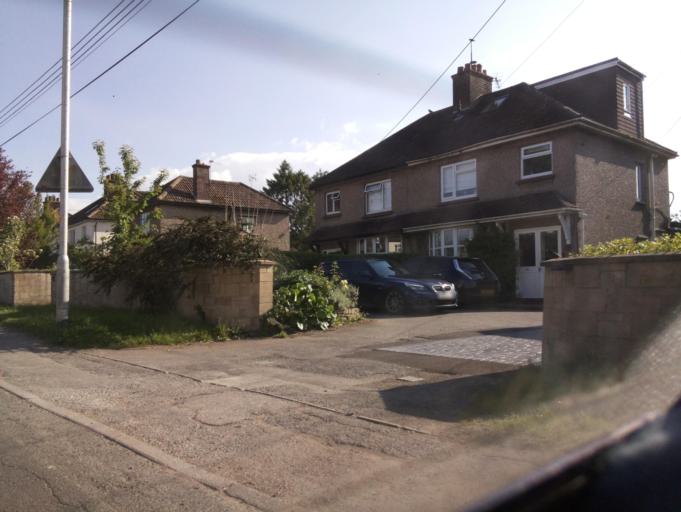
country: GB
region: England
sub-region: Wiltshire
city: Chippenham
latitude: 51.4764
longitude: -2.1274
